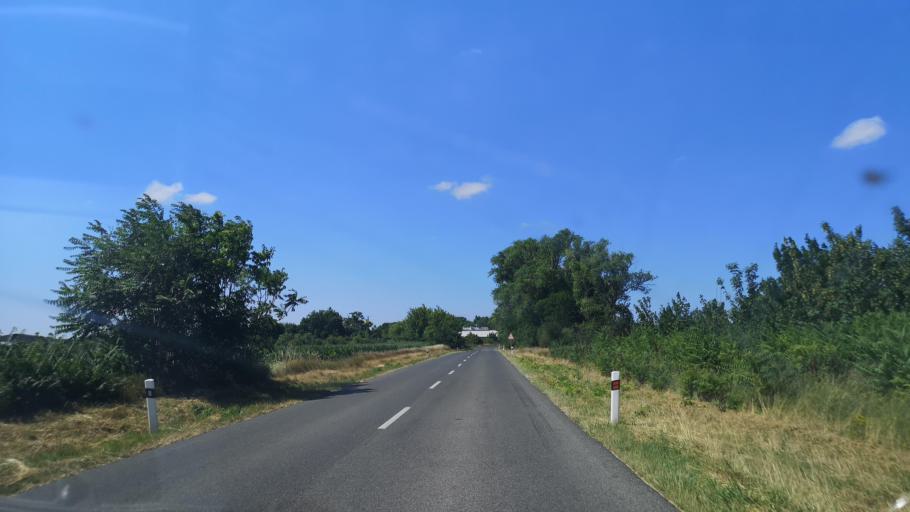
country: SK
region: Trnavsky
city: Dunajska Streda
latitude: 48.0607
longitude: 17.4709
